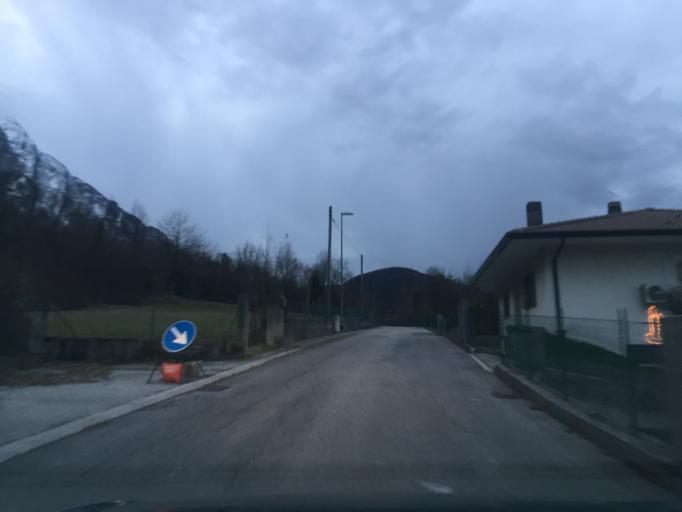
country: IT
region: Friuli Venezia Giulia
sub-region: Provincia di Udine
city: Venzone
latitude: 46.3224
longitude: 13.1387
